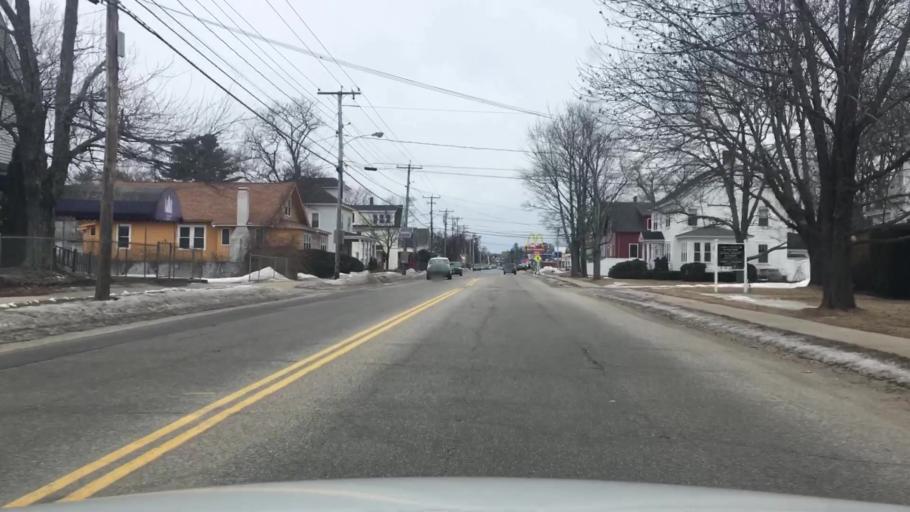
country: US
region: Maine
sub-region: York County
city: Sanford (historical)
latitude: 43.4306
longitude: -70.7691
